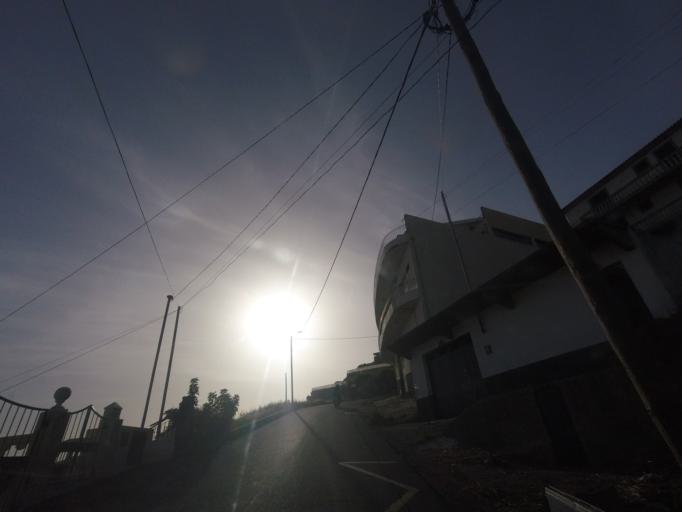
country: PT
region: Madeira
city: Camara de Lobos
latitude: 32.6528
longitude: -16.9890
